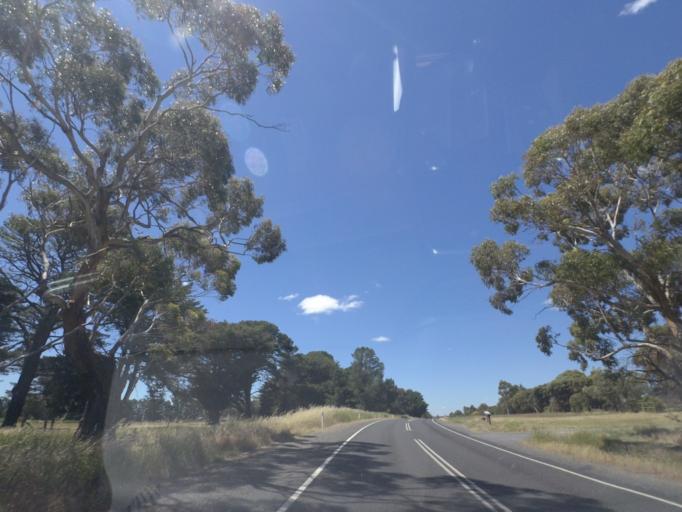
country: AU
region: Victoria
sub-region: Mount Alexander
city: Castlemaine
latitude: -37.2323
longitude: 144.3312
